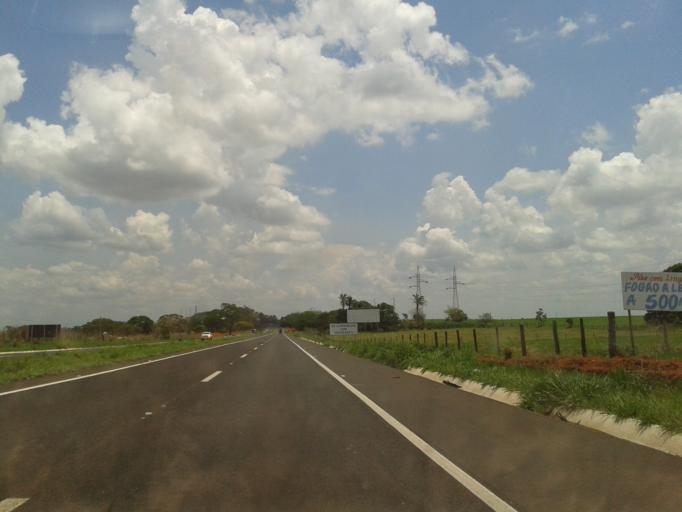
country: BR
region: Minas Gerais
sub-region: Monte Alegre De Minas
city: Monte Alegre de Minas
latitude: -18.8500
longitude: -48.8328
